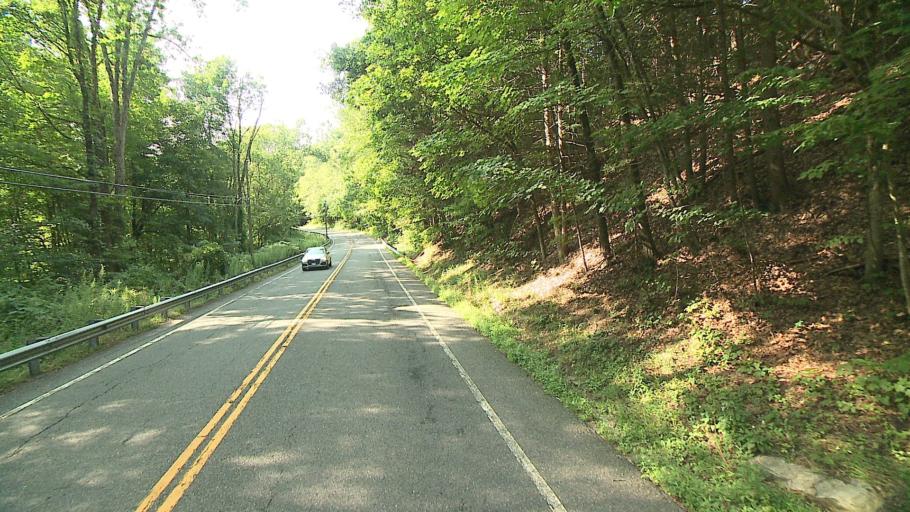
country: US
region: Connecticut
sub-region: Litchfield County
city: Canaan
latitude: 41.9059
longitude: -73.3653
